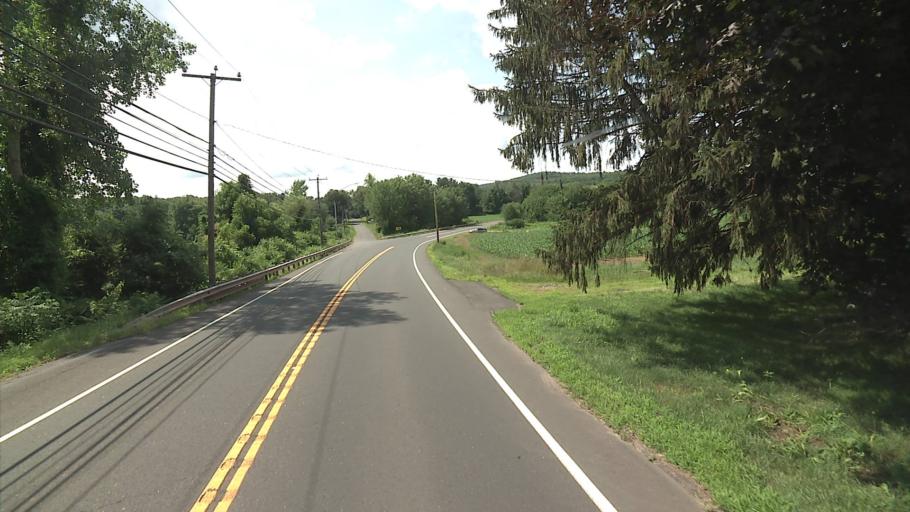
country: US
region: Connecticut
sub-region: Middlesex County
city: Cromwell
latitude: 41.5944
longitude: -72.6060
